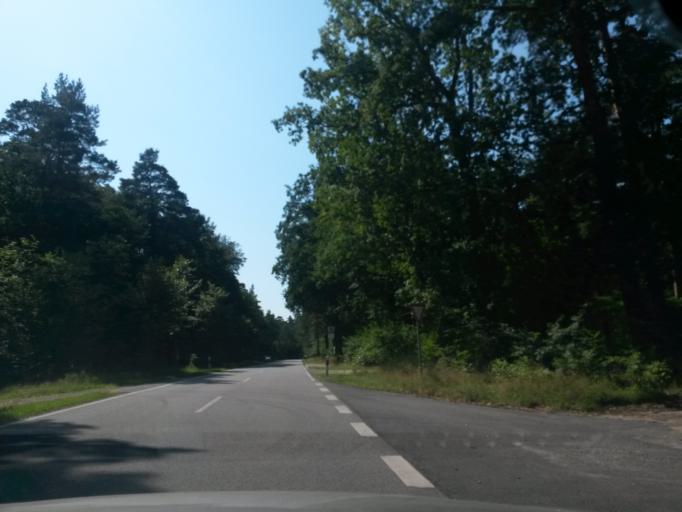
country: DE
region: Brandenburg
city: Marienwerder
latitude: 52.9028
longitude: 13.6450
